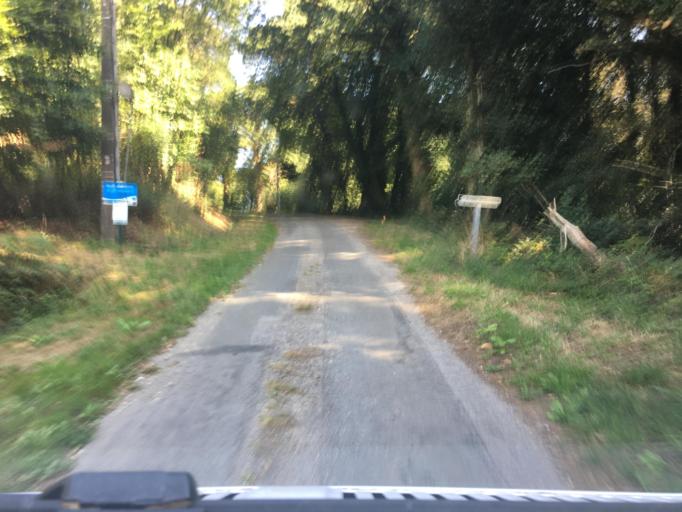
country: FR
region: Brittany
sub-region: Departement des Cotes-d'Armor
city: Mur-de-Bretagne
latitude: 48.2228
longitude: -3.0151
